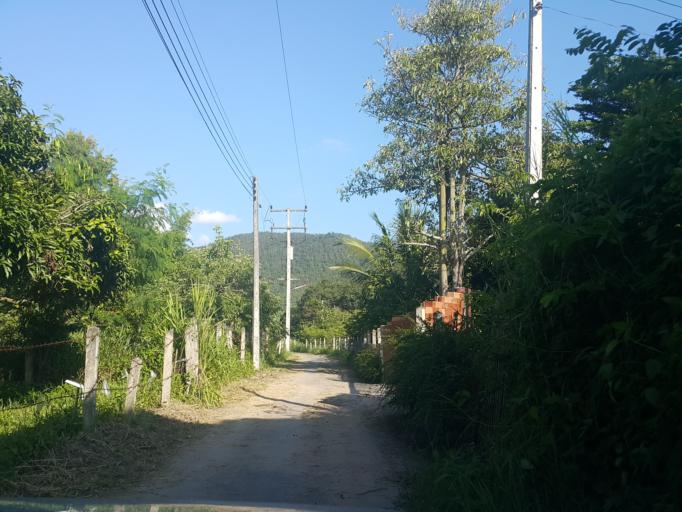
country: TH
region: Chiang Mai
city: Mae On
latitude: 18.7156
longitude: 99.2095
